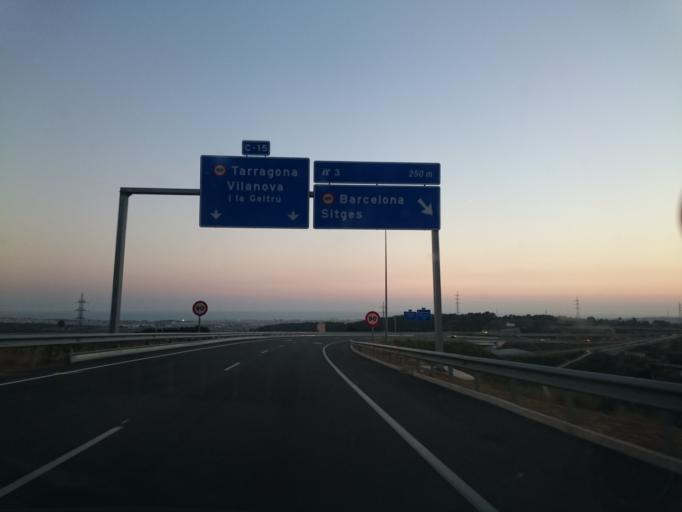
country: ES
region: Catalonia
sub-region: Provincia de Barcelona
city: Sant Pere de Ribes
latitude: 41.2593
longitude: 1.7320
